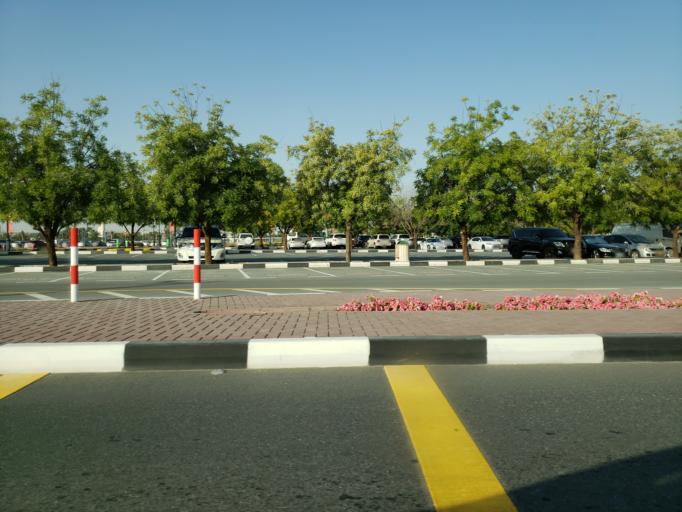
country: AE
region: Ash Shariqah
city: Sharjah
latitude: 25.3201
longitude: 55.5217
